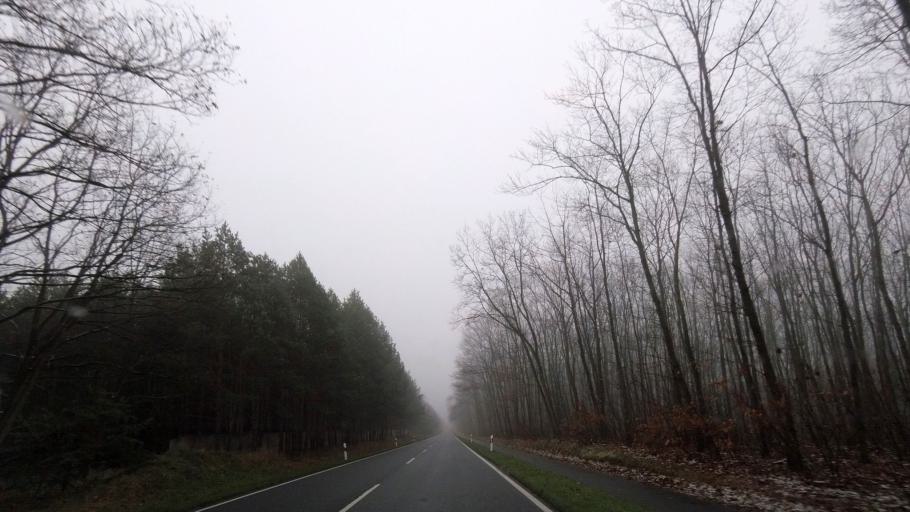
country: DE
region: Brandenburg
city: Niedergorsdorf
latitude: 52.0317
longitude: 12.9553
